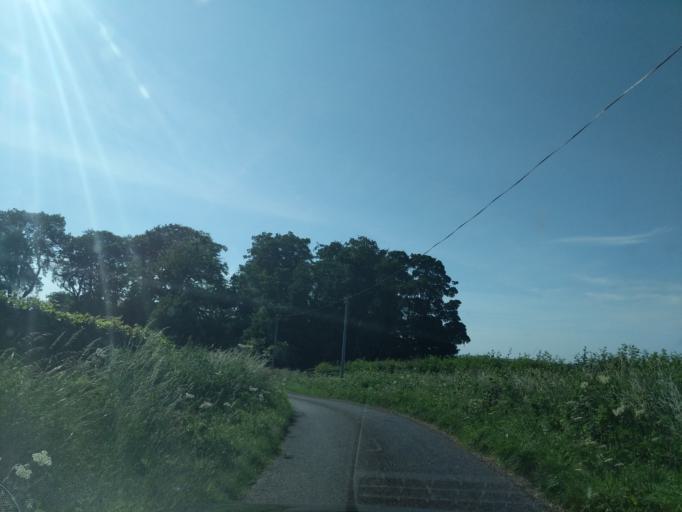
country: GB
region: Scotland
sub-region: East Lothian
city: Ormiston
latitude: 55.8782
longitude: -2.9396
